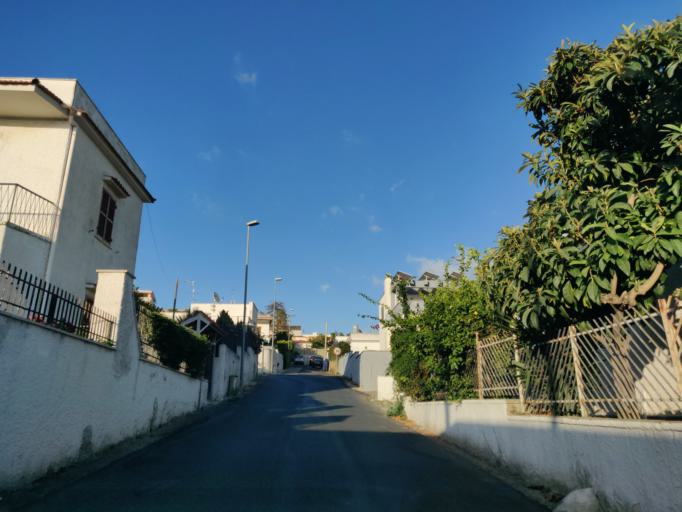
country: IT
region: Latium
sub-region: Citta metropolitana di Roma Capitale
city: Civitavecchia
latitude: 42.0918
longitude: 11.8115
